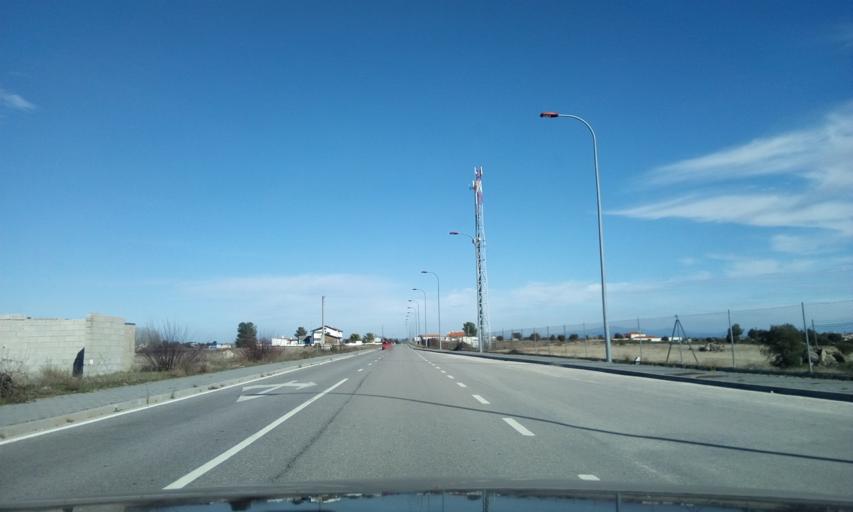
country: ES
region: Castille and Leon
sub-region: Provincia de Salamanca
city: Fuentes de Onoro
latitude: 40.6166
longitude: -6.8532
